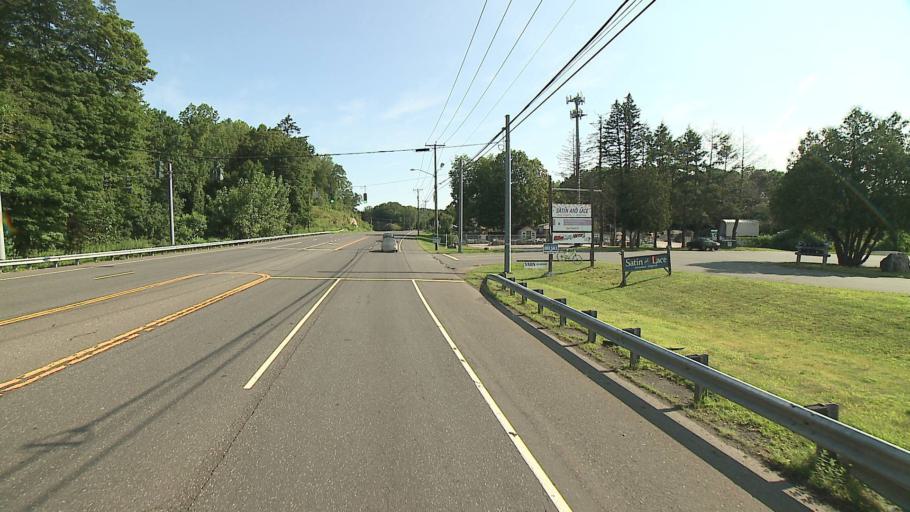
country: US
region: Connecticut
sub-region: Fairfield County
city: Ridgefield
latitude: 41.3354
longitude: -73.4716
